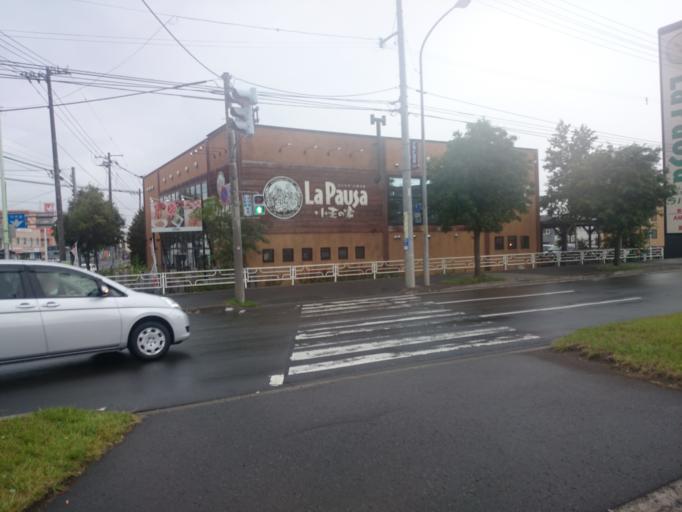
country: JP
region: Hokkaido
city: Sapporo
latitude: 43.0559
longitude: 141.4051
